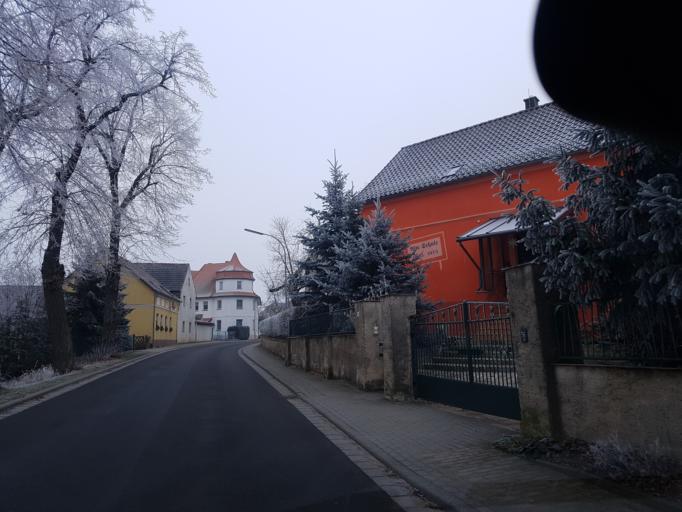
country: DE
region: Brandenburg
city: Muhlberg
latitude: 51.4233
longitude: 13.2620
